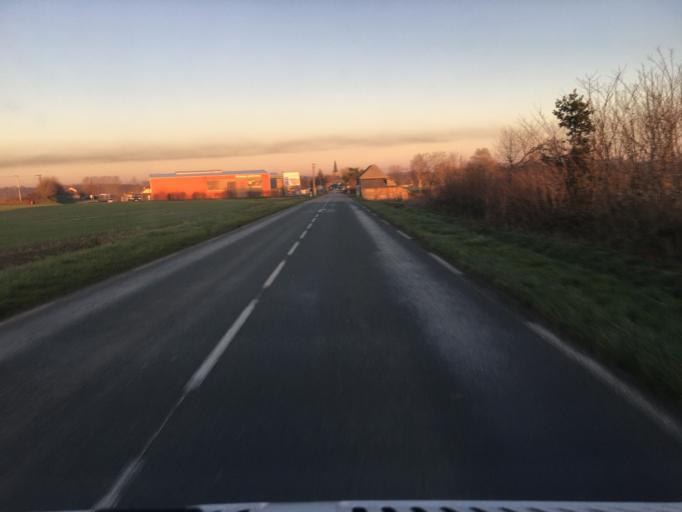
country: FR
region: Haute-Normandie
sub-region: Departement de l'Eure
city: Manneville-sur-Risle
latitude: 49.3789
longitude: 0.5632
